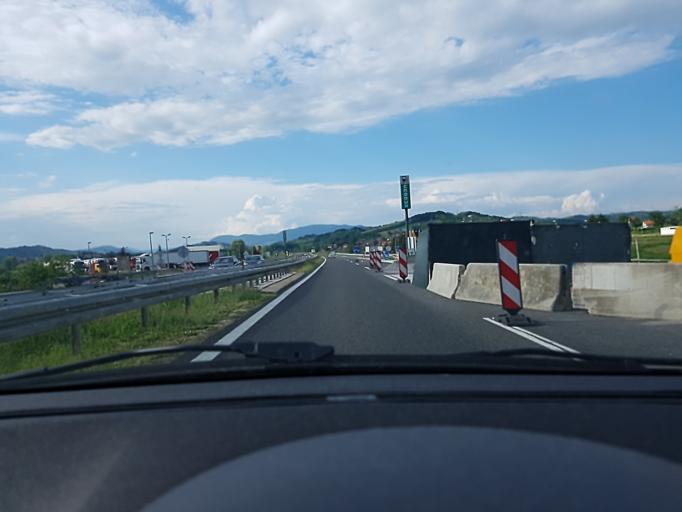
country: HR
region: Krapinsko-Zagorska
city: Zabok
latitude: 46.0655
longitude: 15.9196
